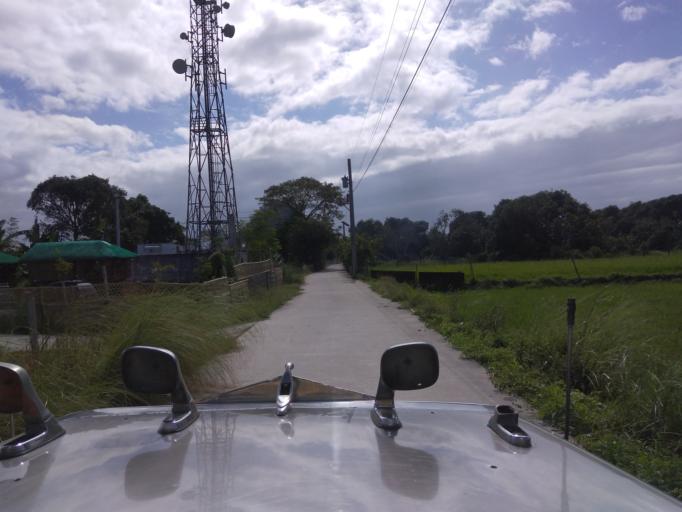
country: PH
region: Central Luzon
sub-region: Province of Pampanga
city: San Patricio
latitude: 15.0896
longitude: 120.7158
